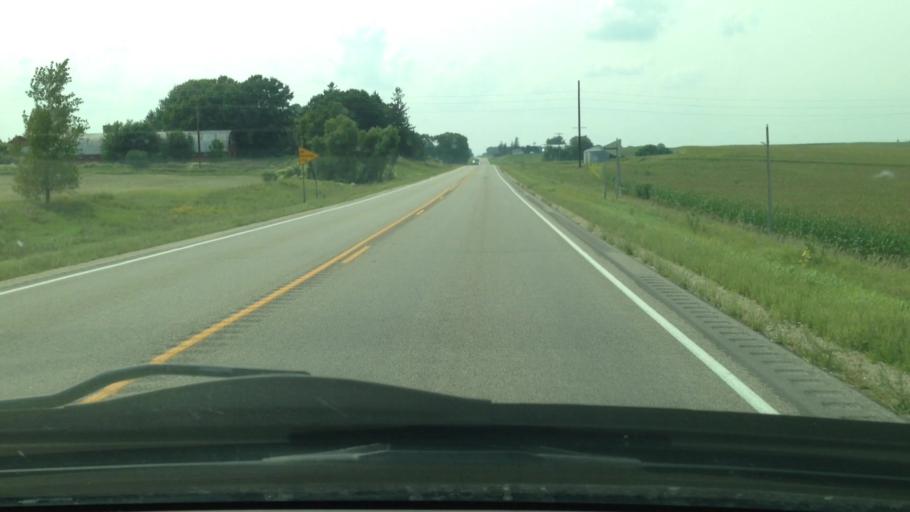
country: US
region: Minnesota
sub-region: Wabasha County
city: Plainview
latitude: 44.1651
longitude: -92.1917
